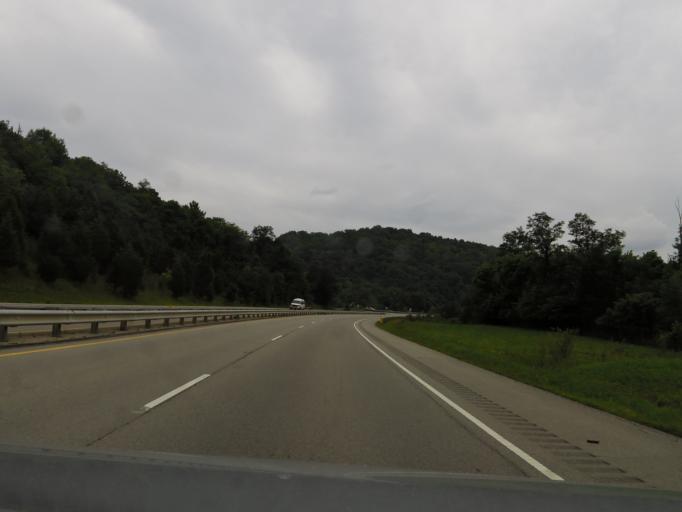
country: US
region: Ohio
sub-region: Brown County
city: Ripley
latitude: 38.7552
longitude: -83.8267
